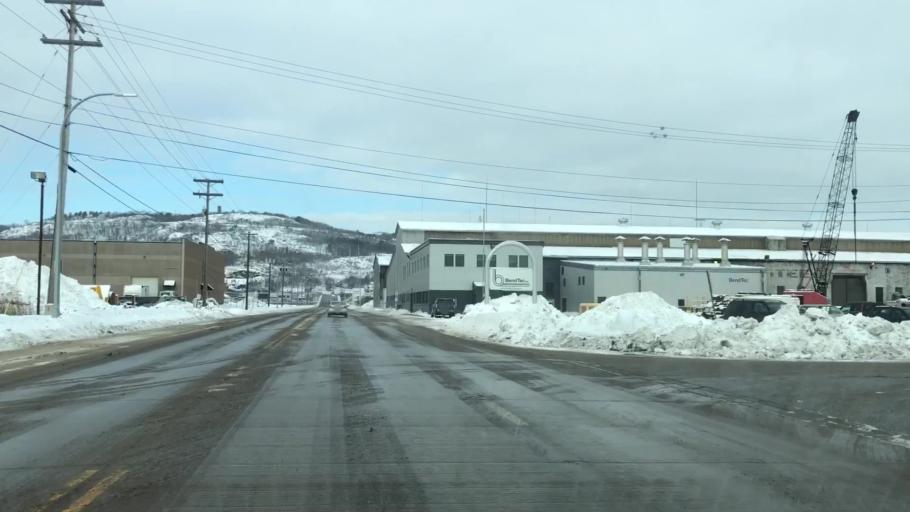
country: US
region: Minnesota
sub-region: Saint Louis County
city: Duluth
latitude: 46.7633
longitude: -92.1119
